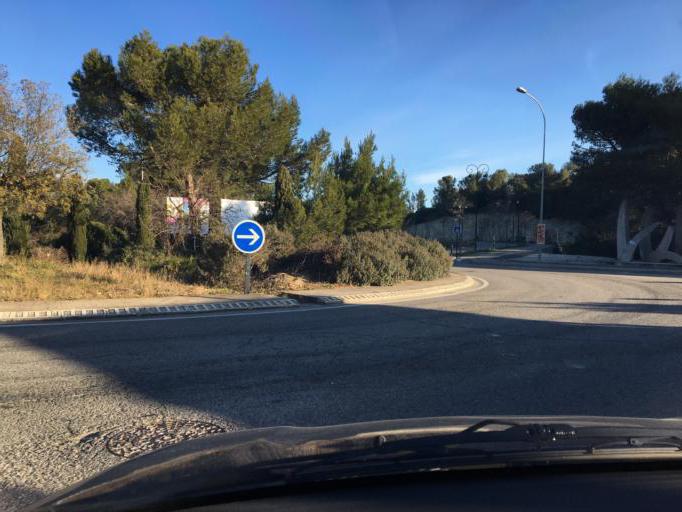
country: FR
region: Languedoc-Roussillon
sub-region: Departement du Gard
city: Villeneuve-les-Avignon
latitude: 43.9795
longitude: 4.7856
